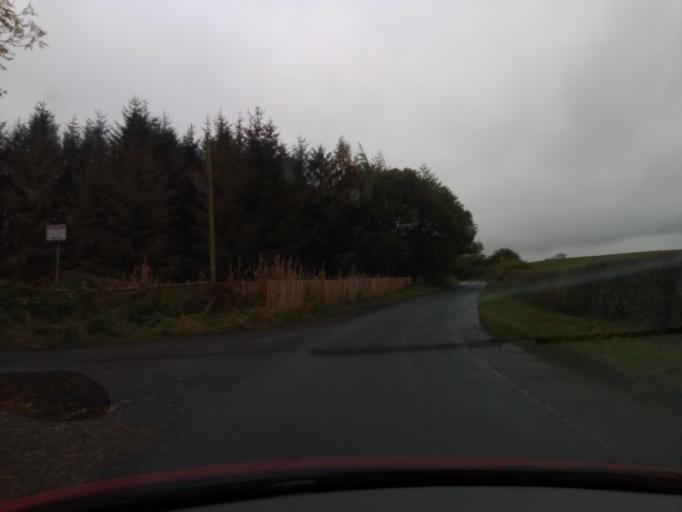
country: GB
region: Scotland
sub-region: The Scottish Borders
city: Melrose
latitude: 55.5110
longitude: -2.7506
